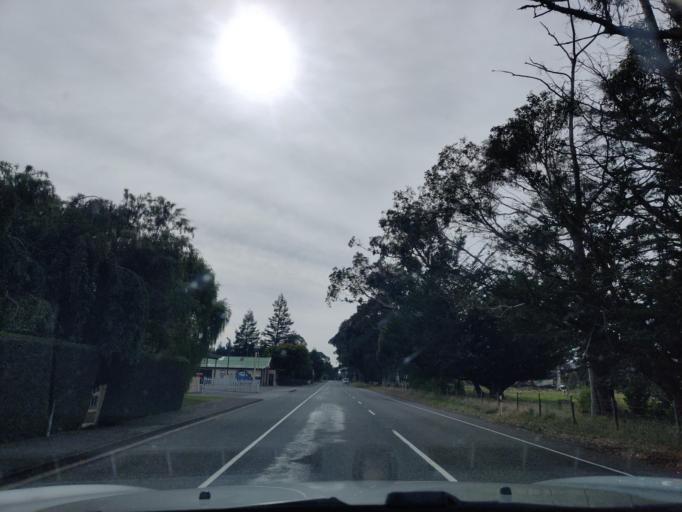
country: NZ
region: Nelson
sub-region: Nelson City
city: Nelson
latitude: -41.5631
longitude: 173.5350
